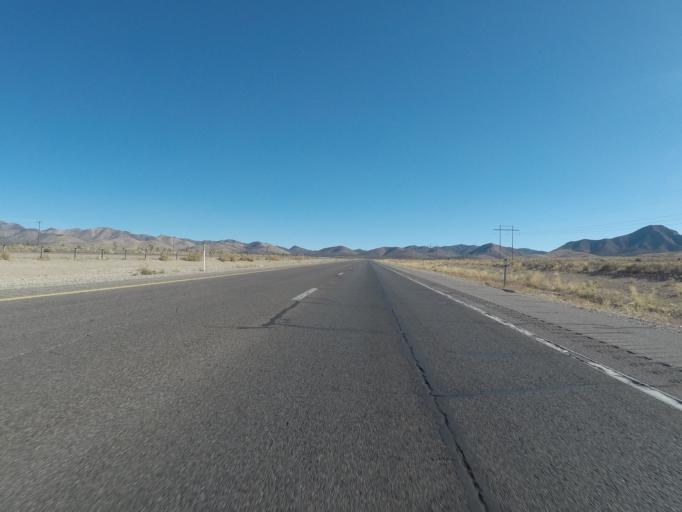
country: US
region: Nevada
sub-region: Clark County
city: Sandy Valley
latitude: 36.0187
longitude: -115.5598
